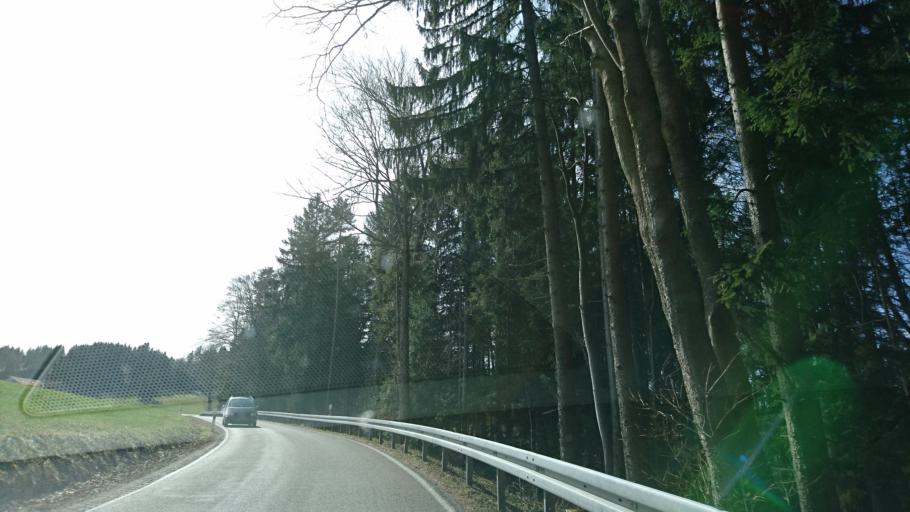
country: DE
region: Bavaria
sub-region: Upper Bavaria
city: Bernbeuren
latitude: 47.7348
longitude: 10.7533
